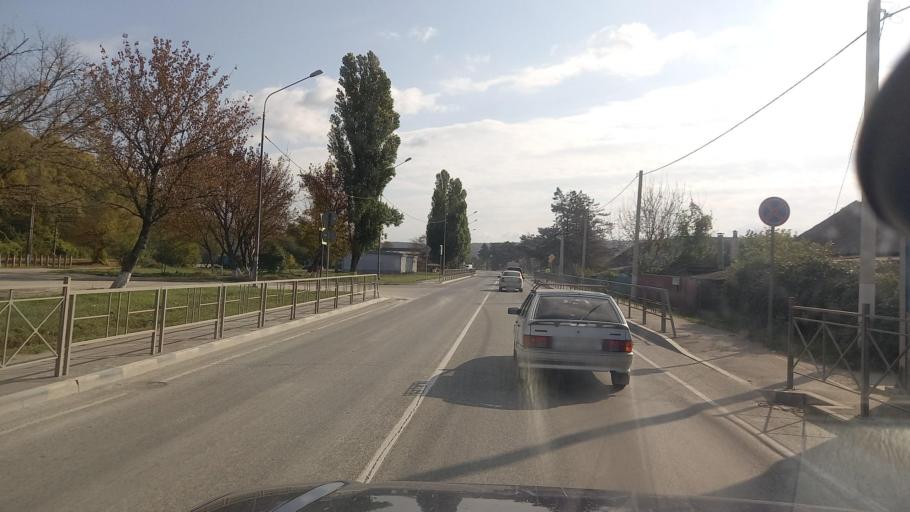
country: RU
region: Krasnodarskiy
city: Krymsk
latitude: 44.8690
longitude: 37.8590
